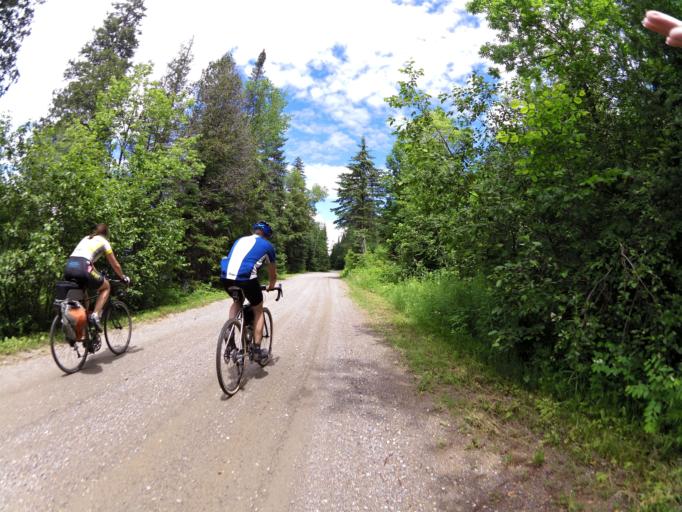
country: CA
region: Ontario
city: Renfrew
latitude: 45.1252
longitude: -76.6880
